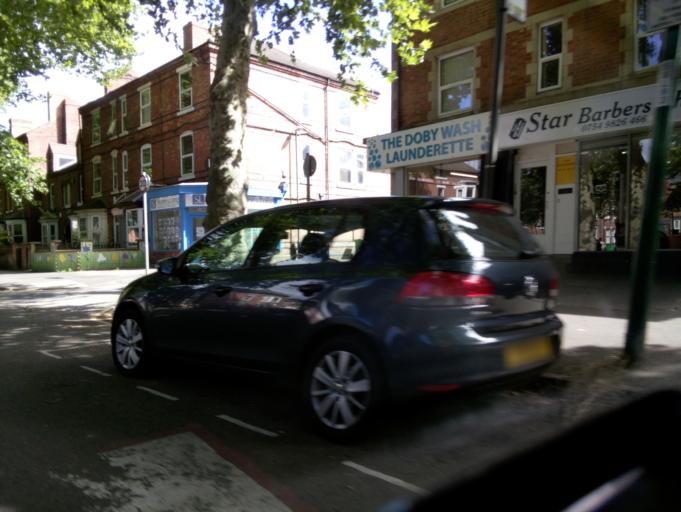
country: GB
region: England
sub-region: Nottingham
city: Nottingham
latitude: 52.9478
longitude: -1.1741
